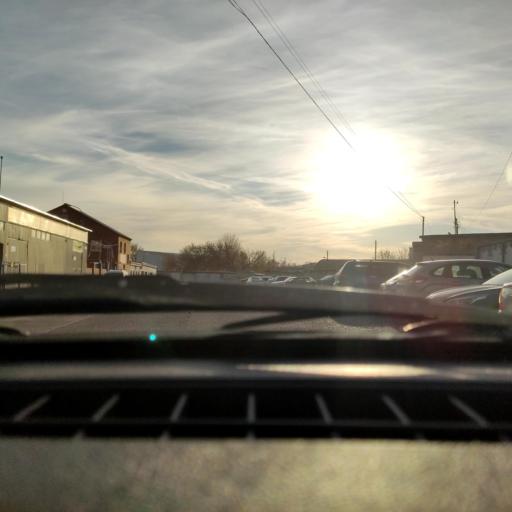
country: RU
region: Bashkortostan
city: Ufa
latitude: 54.8009
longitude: 56.0923
